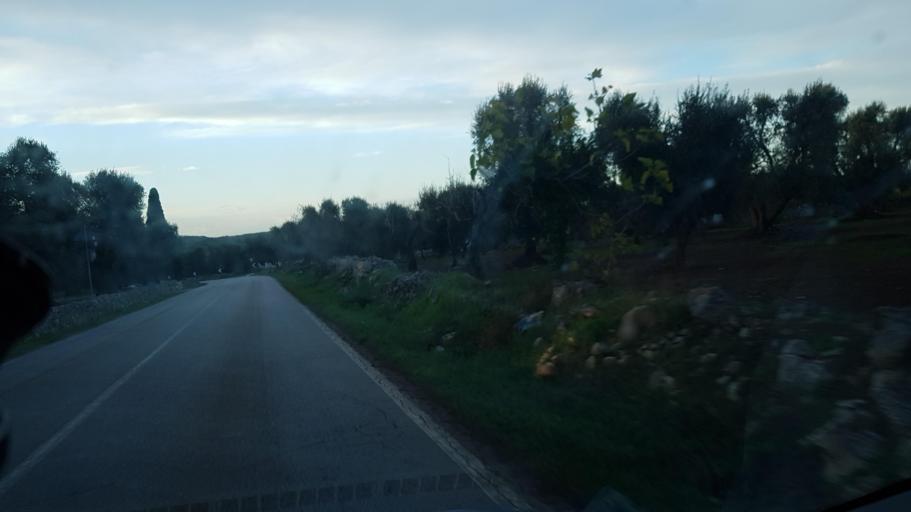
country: IT
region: Apulia
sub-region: Provincia di Brindisi
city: Ceglie Messapica
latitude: 40.6442
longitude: 17.5549
